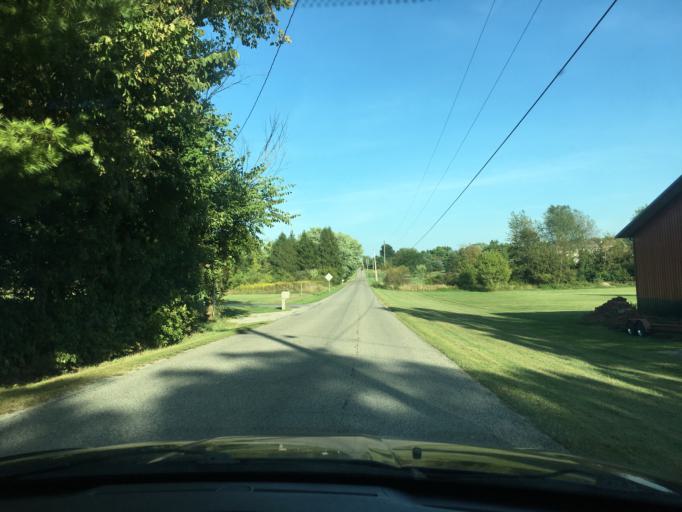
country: US
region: Ohio
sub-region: Logan County
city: West Liberty
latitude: 40.3024
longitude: -83.7581
